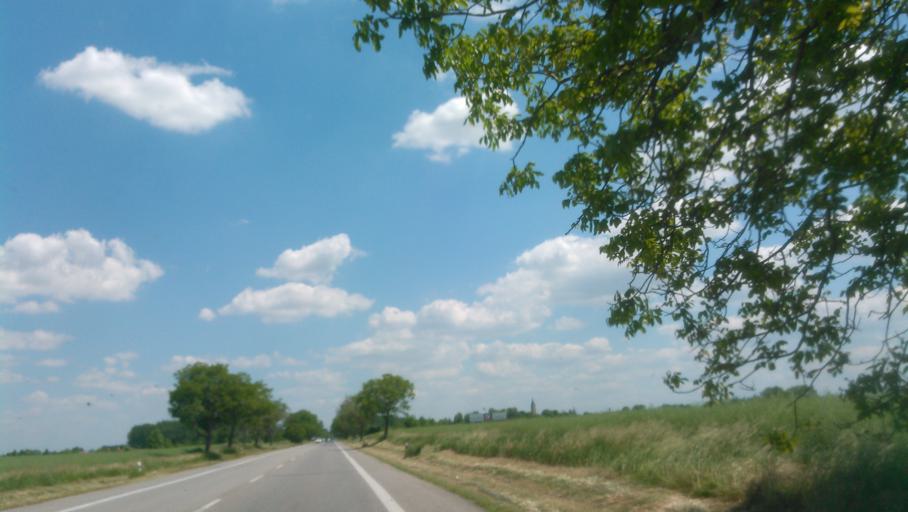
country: SK
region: Trnavsky
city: Samorin
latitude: 48.0093
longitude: 17.3579
